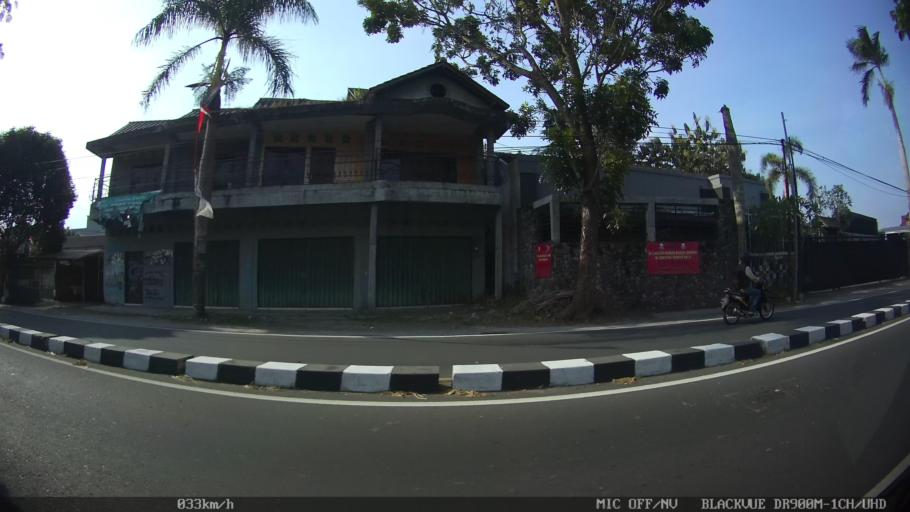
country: ID
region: Daerah Istimewa Yogyakarta
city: Kasihan
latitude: -7.8218
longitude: 110.3290
